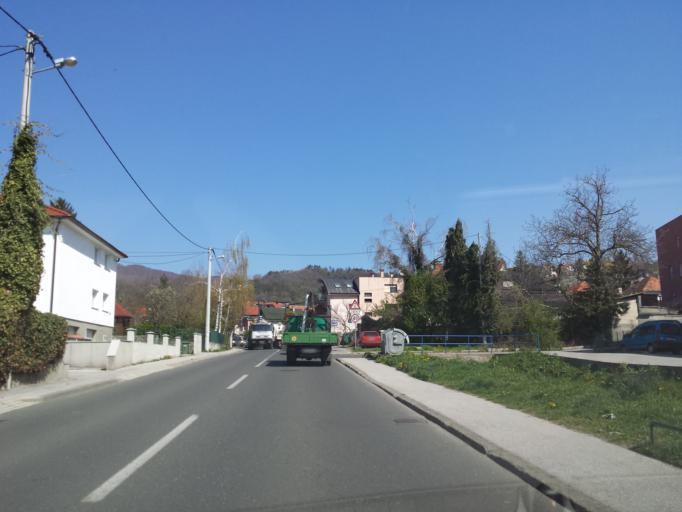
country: HR
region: Grad Zagreb
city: Zagreb
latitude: 45.8531
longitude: 15.9748
